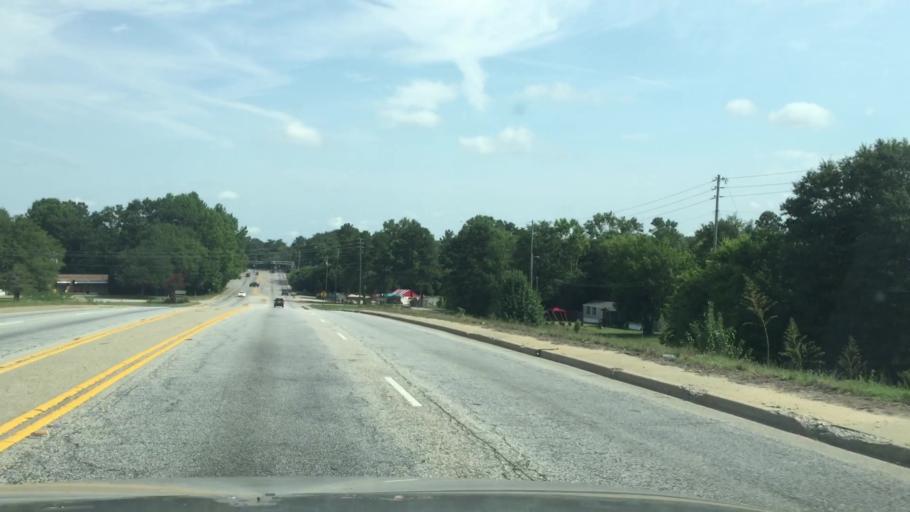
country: US
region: South Carolina
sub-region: Sumter County
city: South Sumter
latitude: 33.9066
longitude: -80.3539
